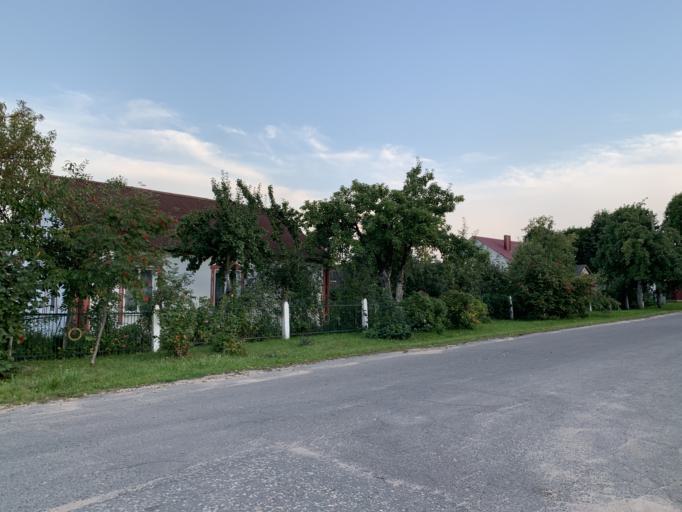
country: BY
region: Minsk
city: Nyasvizh
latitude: 53.2188
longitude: 26.6942
